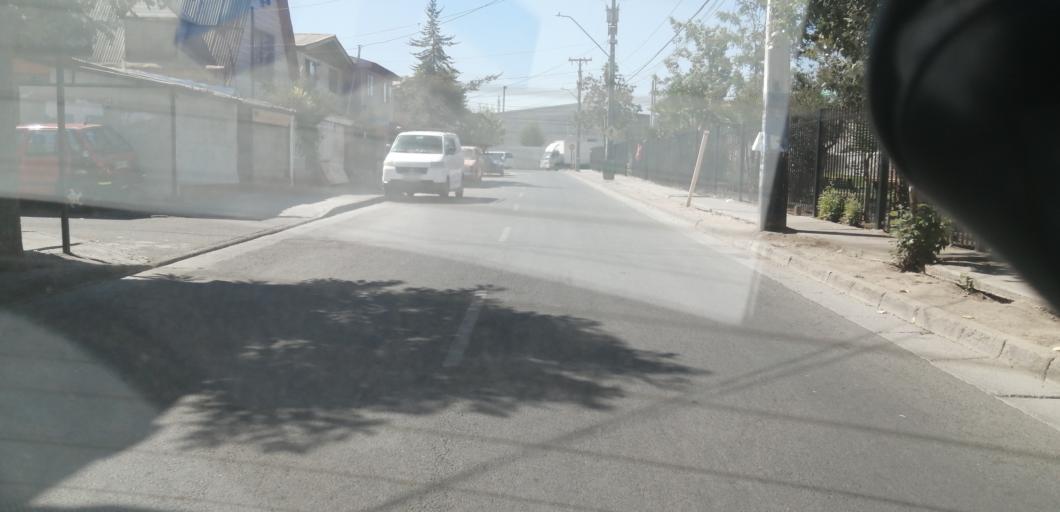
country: CL
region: Santiago Metropolitan
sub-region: Provincia de Santiago
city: Lo Prado
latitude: -33.4393
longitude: -70.7646
